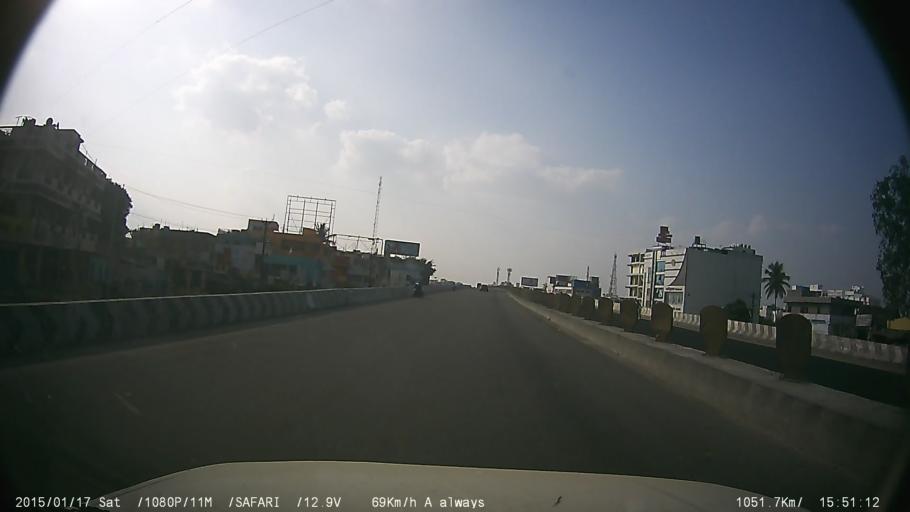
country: IN
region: Tamil Nadu
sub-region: Krishnagiri
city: Hosur
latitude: 12.7340
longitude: 77.8322
